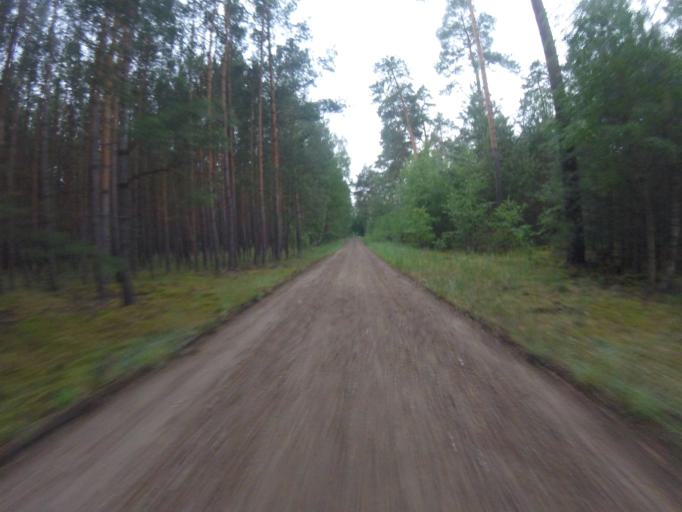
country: DE
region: Brandenburg
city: Gross Koris
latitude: 52.1991
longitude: 13.6960
